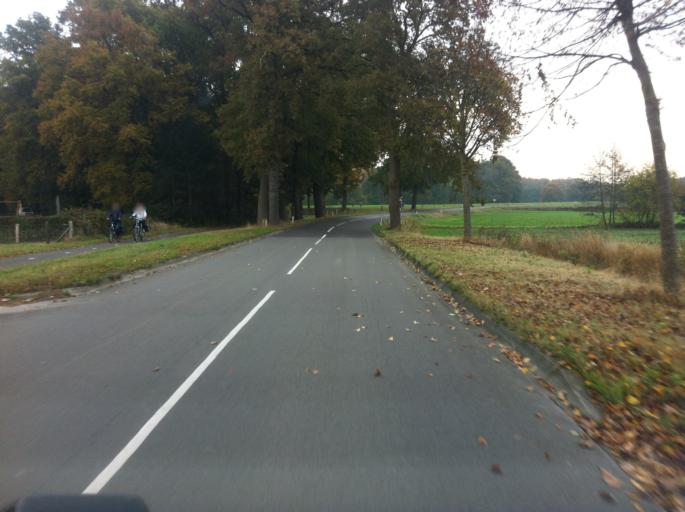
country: NL
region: Overijssel
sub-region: Gemeente Enschede
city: Enschede
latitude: 52.1432
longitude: 6.8419
